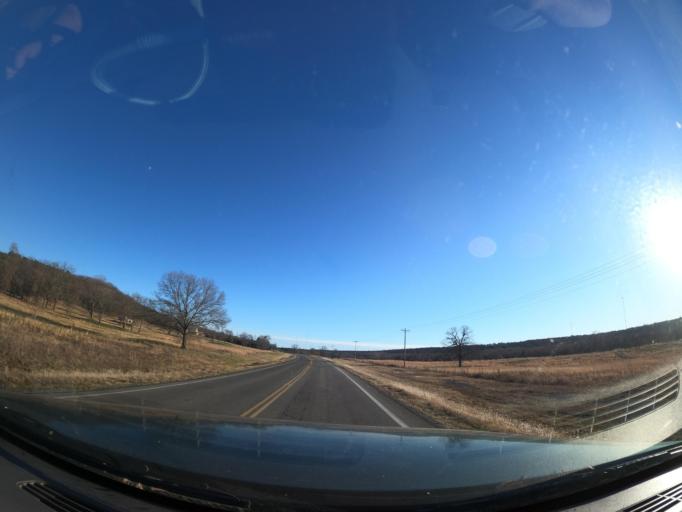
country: US
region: Oklahoma
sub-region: Latimer County
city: Wilburton
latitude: 34.9341
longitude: -95.3401
